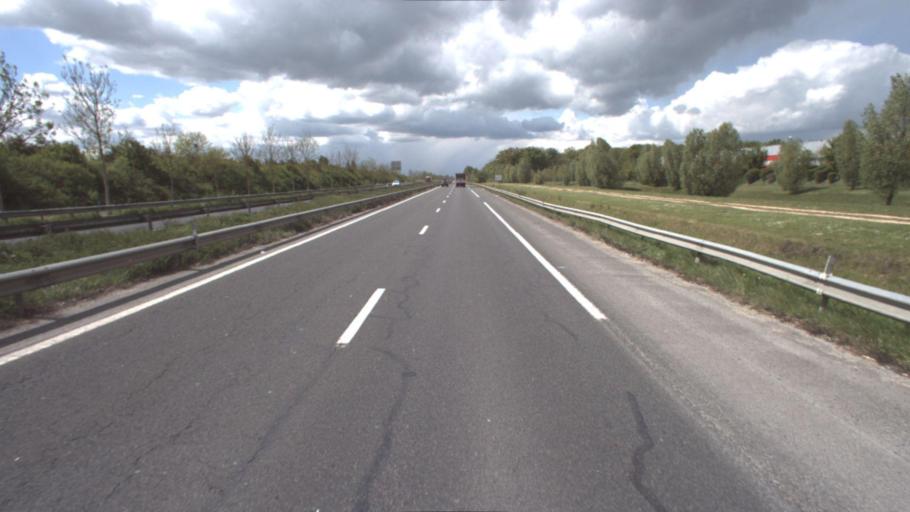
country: FR
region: Ile-de-France
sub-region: Departement de Seine-et-Marne
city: Fontenay-Tresigny
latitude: 48.7222
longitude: 2.8364
